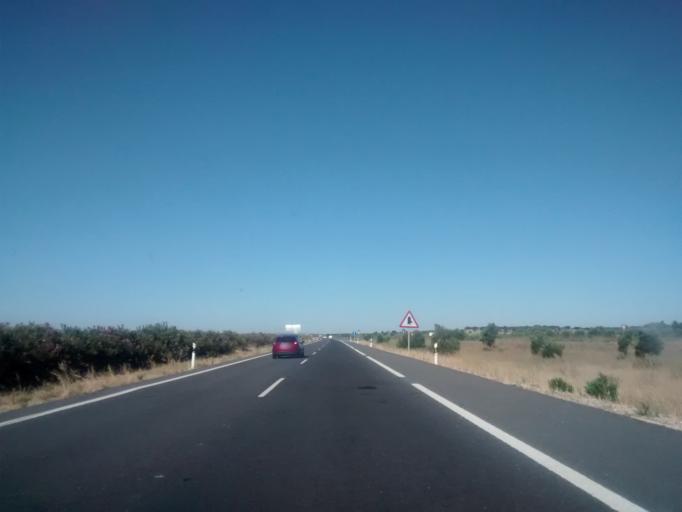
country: ES
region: Andalusia
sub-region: Provincia de Huelva
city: Aljaraque
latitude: 37.3355
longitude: -7.0242
